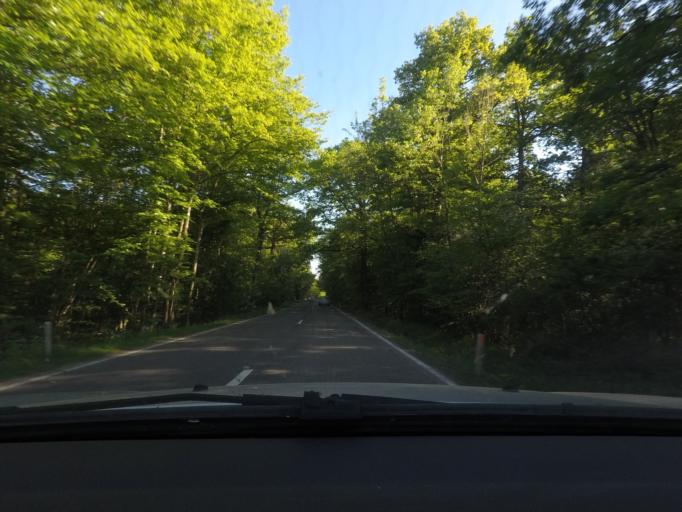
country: BE
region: Wallonia
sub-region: Province du Luxembourg
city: Wellin
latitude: 50.1833
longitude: 5.1208
